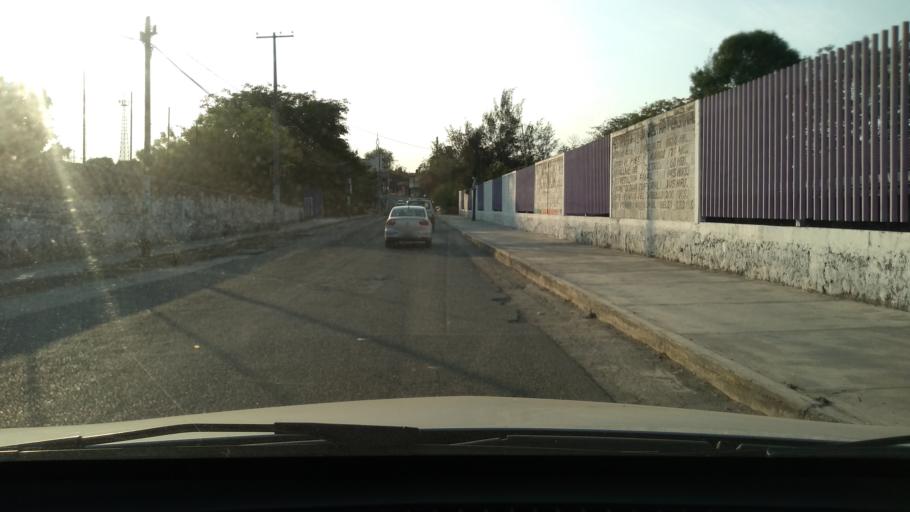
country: MX
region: Morelos
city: Puente de Ixtla
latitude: 18.6216
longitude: -99.3184
